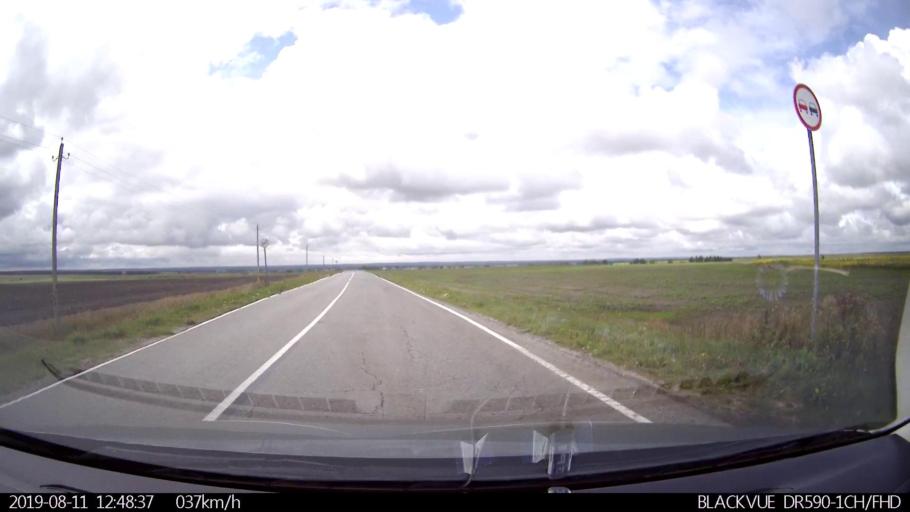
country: RU
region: Ulyanovsk
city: Ignatovka
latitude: 53.8742
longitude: 47.6978
